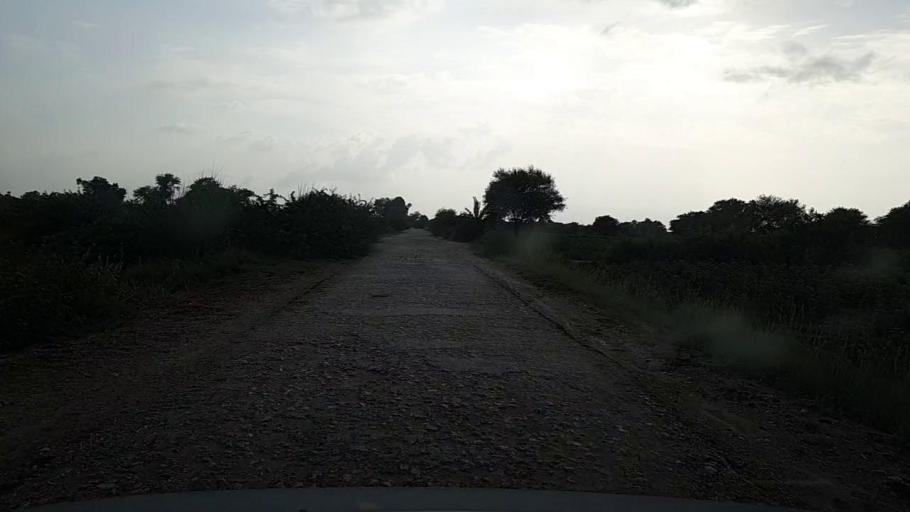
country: PK
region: Sindh
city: Pad Idan
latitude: 26.7949
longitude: 68.2307
